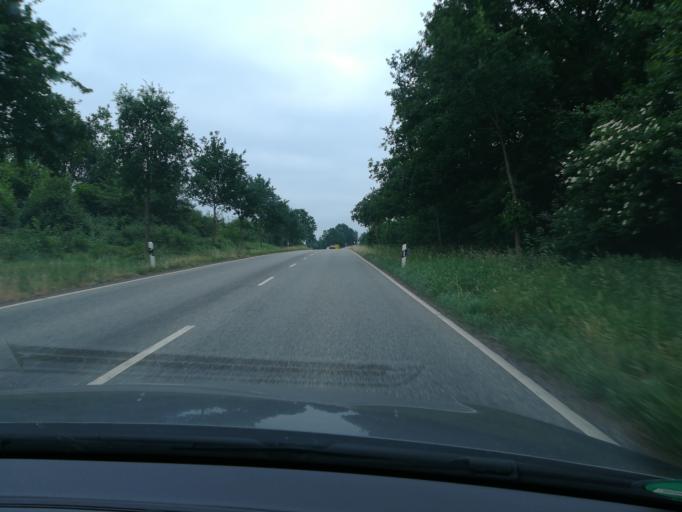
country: DE
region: Schleswig-Holstein
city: Siek
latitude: 53.6371
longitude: 10.3068
